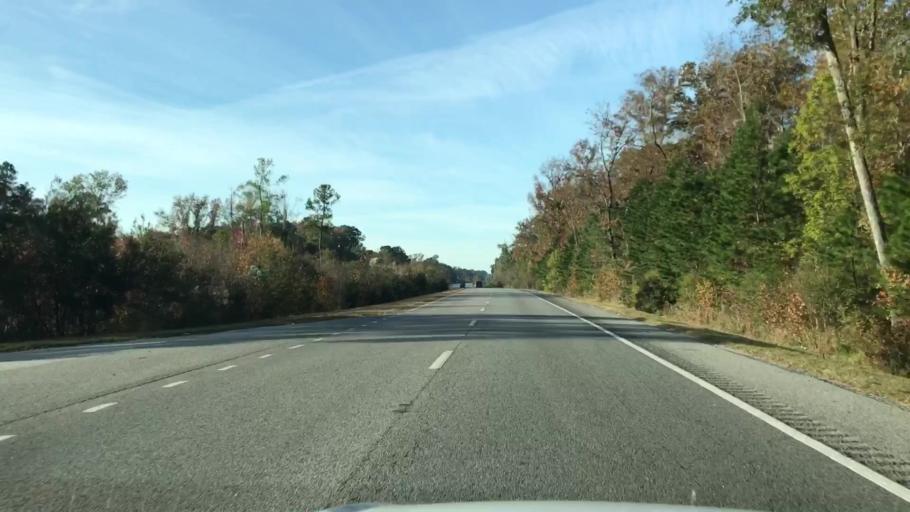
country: US
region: South Carolina
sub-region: Hampton County
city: Yemassee
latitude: 32.6271
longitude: -80.7286
